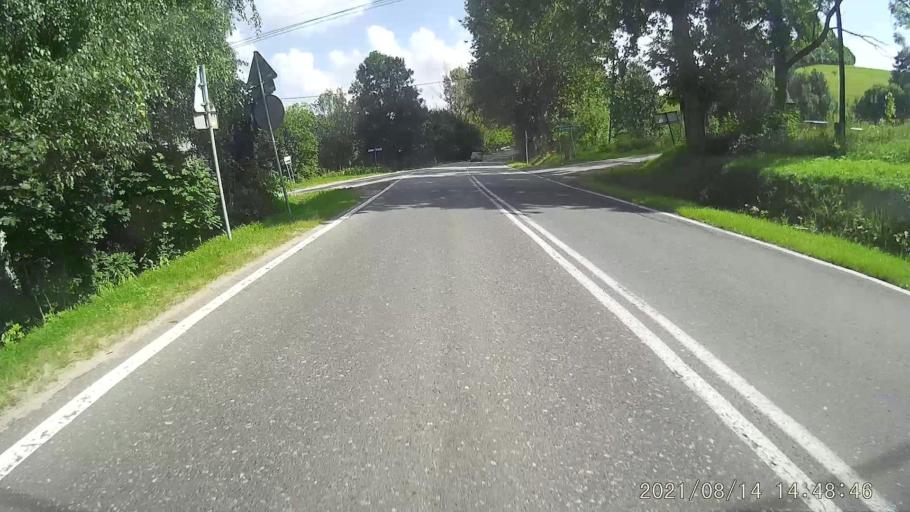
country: PL
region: Lower Silesian Voivodeship
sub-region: Powiat walbrzyski
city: Gluszyca Gorna
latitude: 50.6367
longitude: 16.3936
